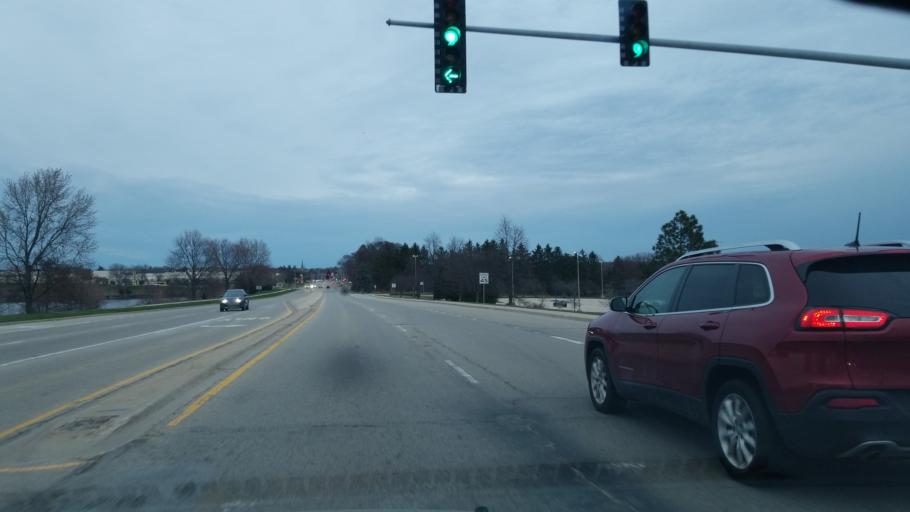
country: US
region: Illinois
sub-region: Kane County
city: Sleepy Hollow
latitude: 42.0991
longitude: -88.2968
